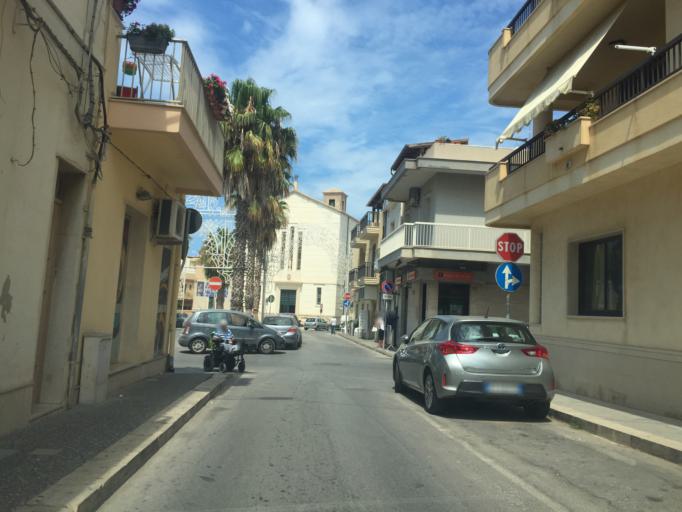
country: IT
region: Sicily
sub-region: Ragusa
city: Scoglitti
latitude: 36.8914
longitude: 14.4310
